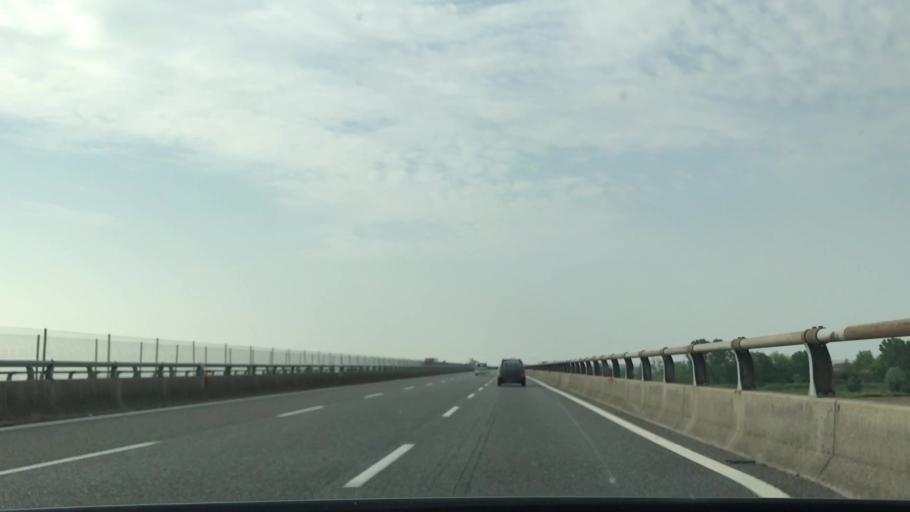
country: IT
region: Piedmont
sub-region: Provincia di Vercelli
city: Prarolo
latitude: 45.3028
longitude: 8.4706
